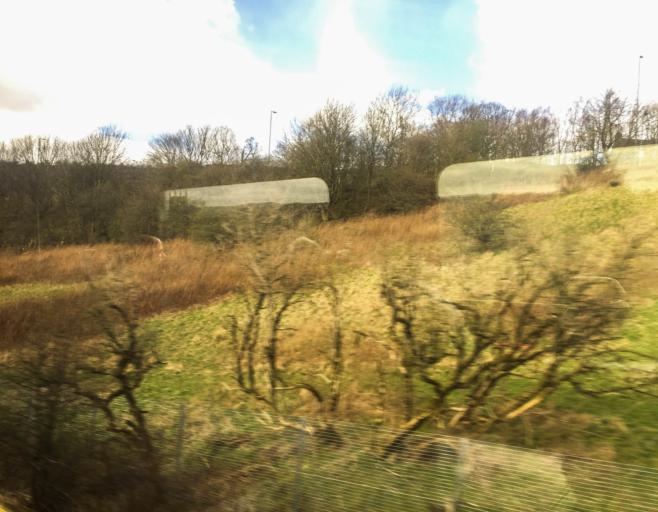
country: GB
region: Scotland
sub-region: West Dunbartonshire
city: Old Kilpatrick
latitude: 55.9266
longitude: -4.4576
